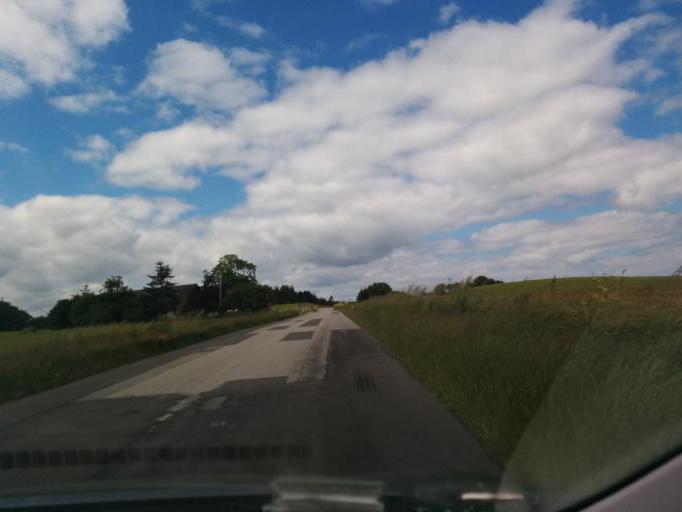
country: DK
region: Central Jutland
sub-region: Norddjurs Kommune
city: Grenaa
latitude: 56.5088
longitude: 10.7318
